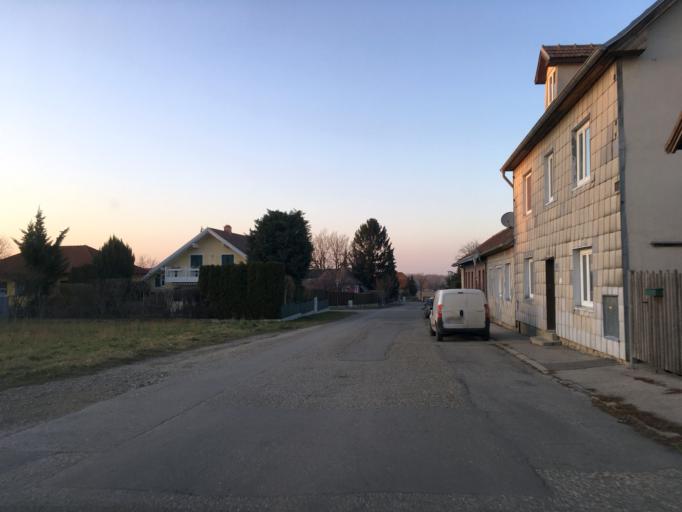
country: AT
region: Lower Austria
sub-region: Politischer Bezirk Tulln
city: Wordern
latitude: 48.3235
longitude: 16.2063
